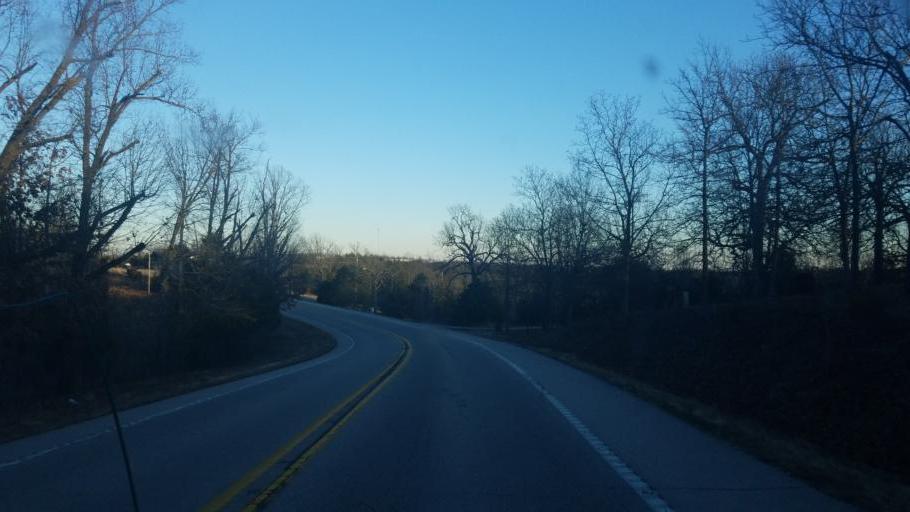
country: US
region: Arkansas
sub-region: Baxter County
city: Mountain Home
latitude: 36.3855
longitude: -92.1843
